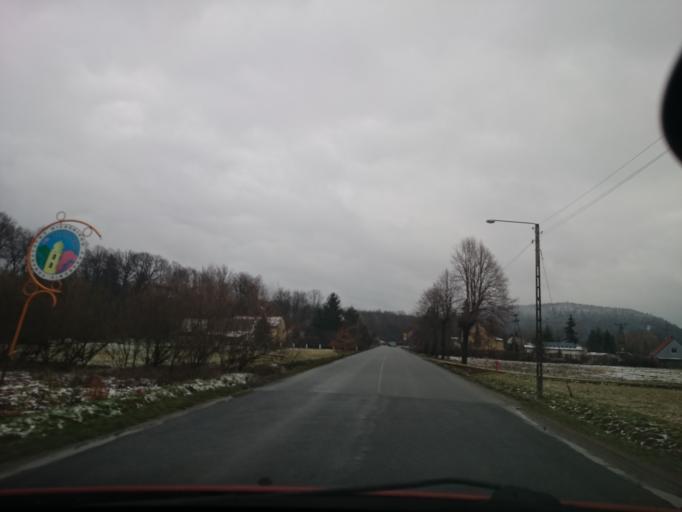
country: PL
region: Lower Silesian Voivodeship
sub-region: Powiat klodzki
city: Klodzko
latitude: 50.3888
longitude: 16.6266
